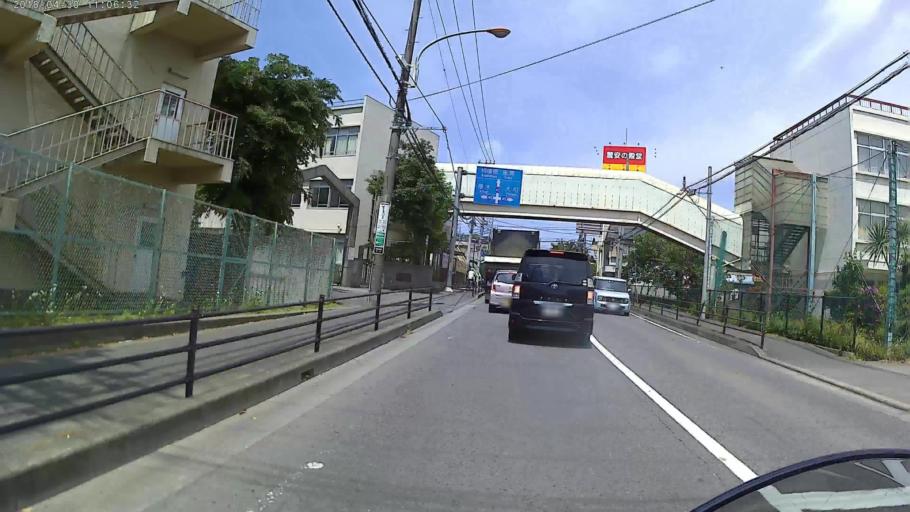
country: JP
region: Kanagawa
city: Minami-rinkan
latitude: 35.4563
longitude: 139.4275
